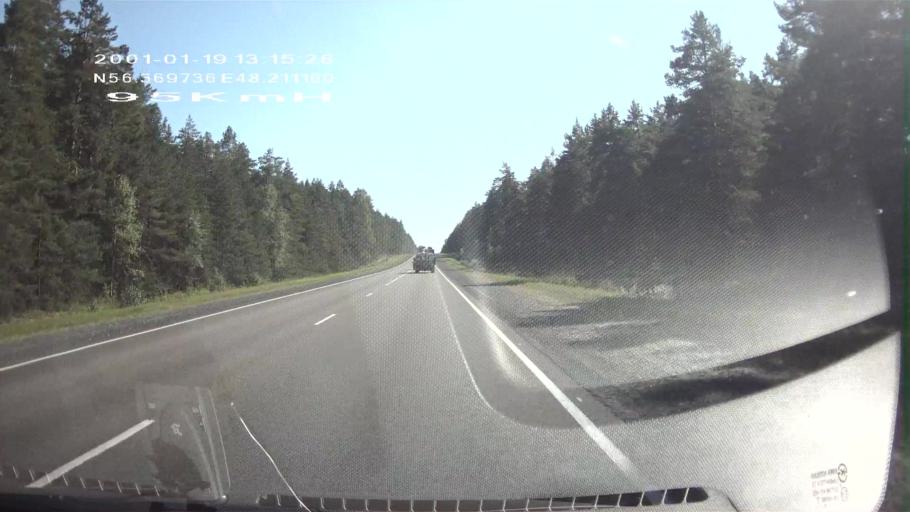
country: RU
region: Mariy-El
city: Suslonger
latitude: 56.3694
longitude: 48.2114
